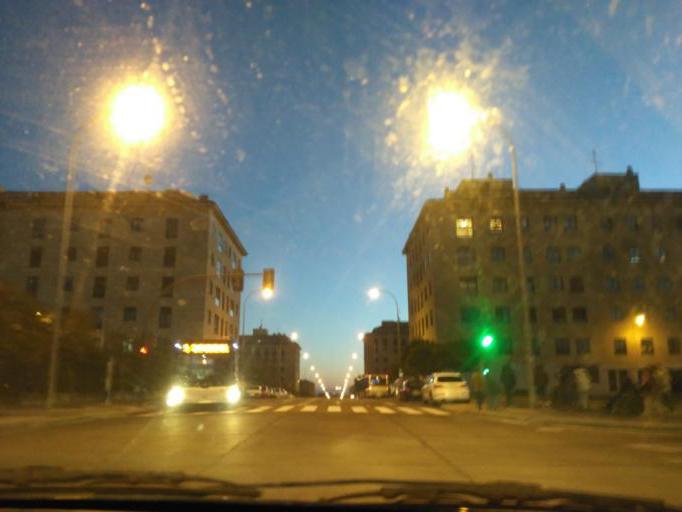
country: ES
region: Castille and Leon
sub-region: Provincia de Salamanca
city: Salamanca
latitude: 40.9830
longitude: -5.6673
